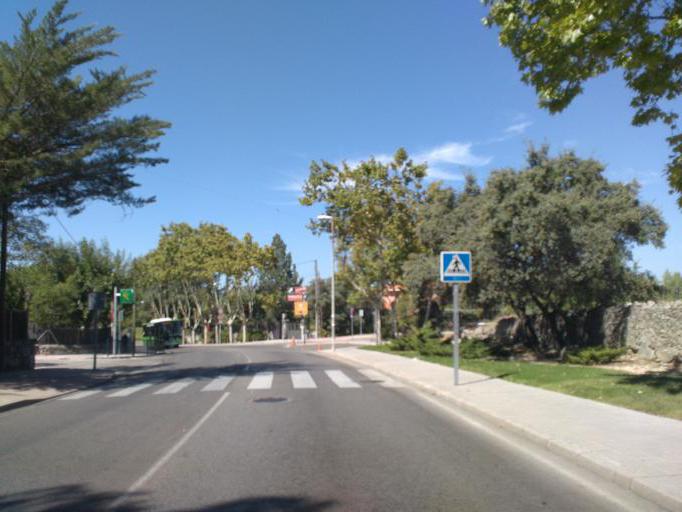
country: ES
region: Madrid
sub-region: Provincia de Madrid
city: Torrelodones
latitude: 40.5768
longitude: -3.9475
